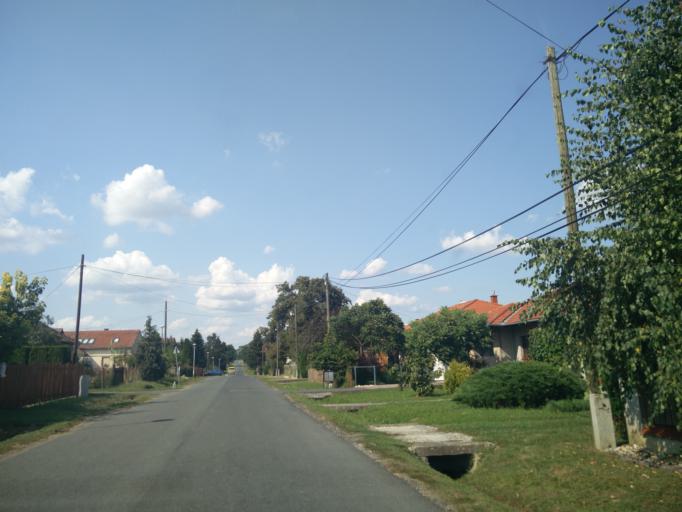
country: HU
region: Zala
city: Zalaegerszeg
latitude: 46.8866
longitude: 16.7933
